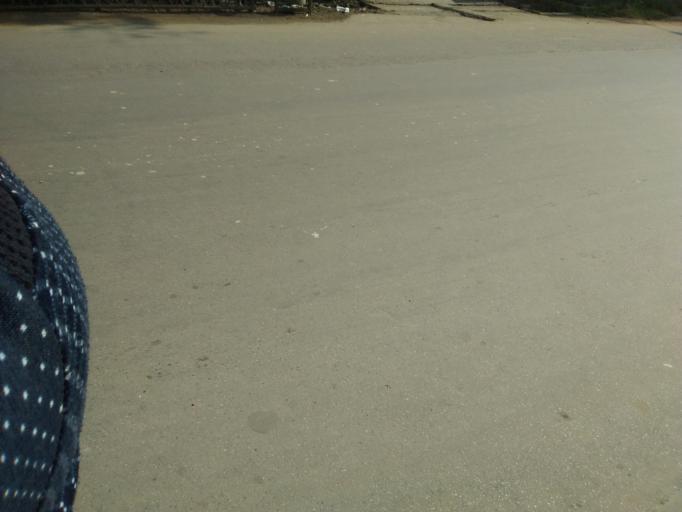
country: BD
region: Khulna
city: Khulna
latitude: 22.8063
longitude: 89.5772
